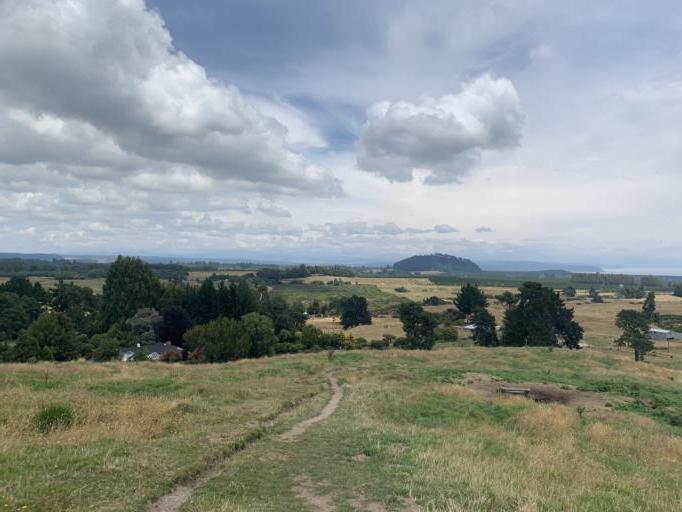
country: NZ
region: Waikato
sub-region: Taupo District
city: Taupo
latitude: -38.7022
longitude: 176.1420
